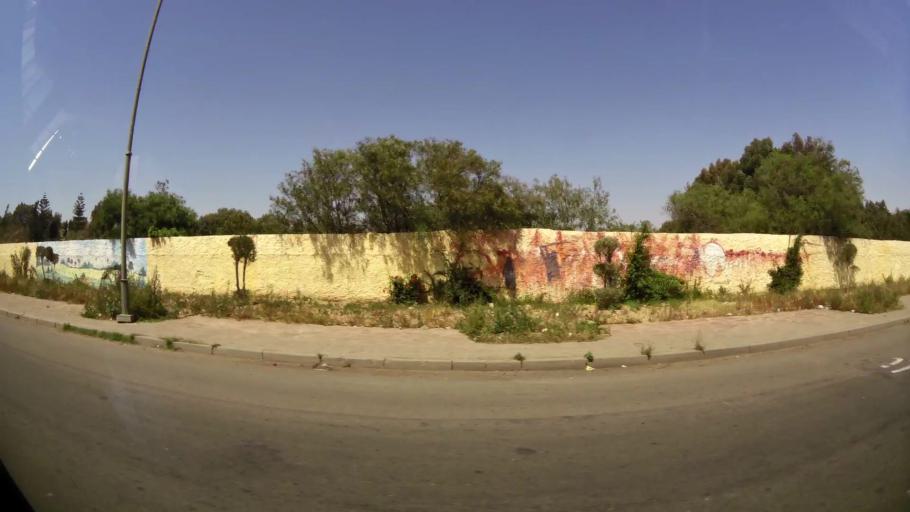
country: MA
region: Souss-Massa-Draa
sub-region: Inezgane-Ait Mellou
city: Inezgane
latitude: 30.3537
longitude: -9.5092
